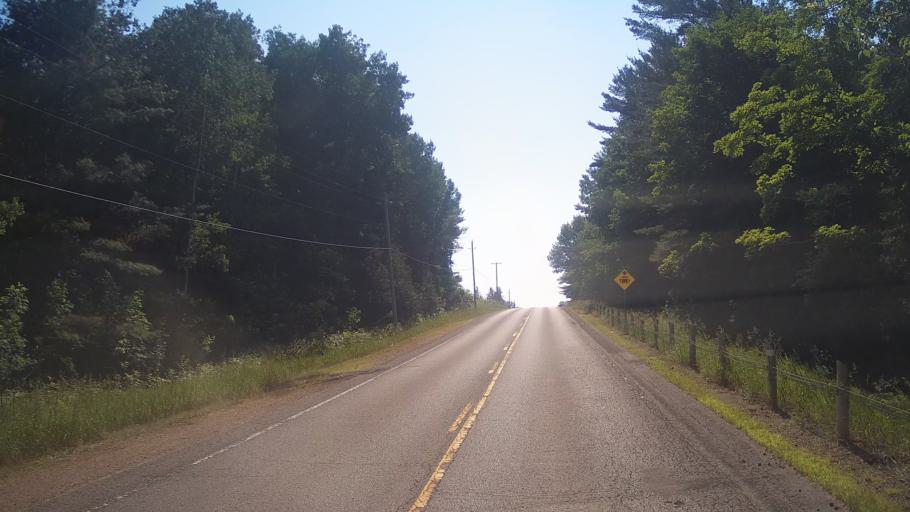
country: CA
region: Ontario
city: Pembroke
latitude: 45.6063
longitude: -77.2181
